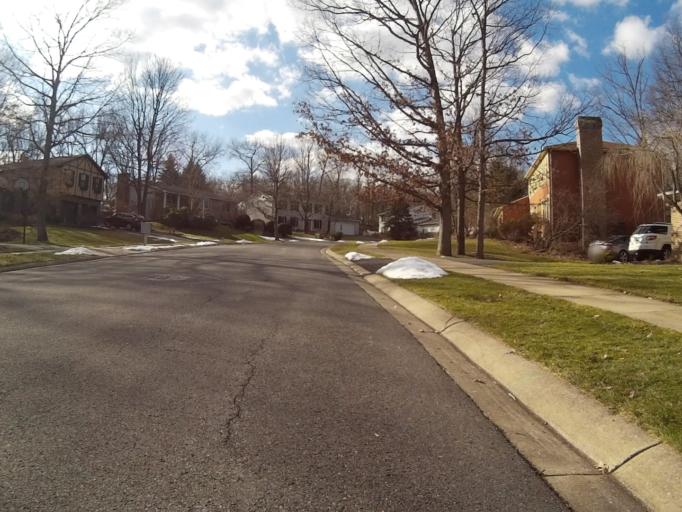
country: US
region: Pennsylvania
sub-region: Centre County
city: Park Forest Village
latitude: 40.7984
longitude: -77.9113
